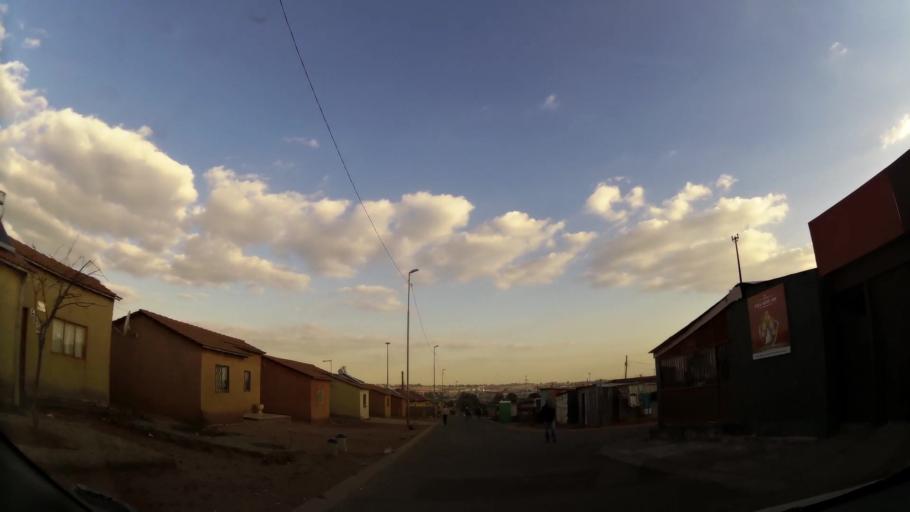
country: ZA
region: Gauteng
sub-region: West Rand District Municipality
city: Krugersdorp
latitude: -26.0786
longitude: 27.7588
